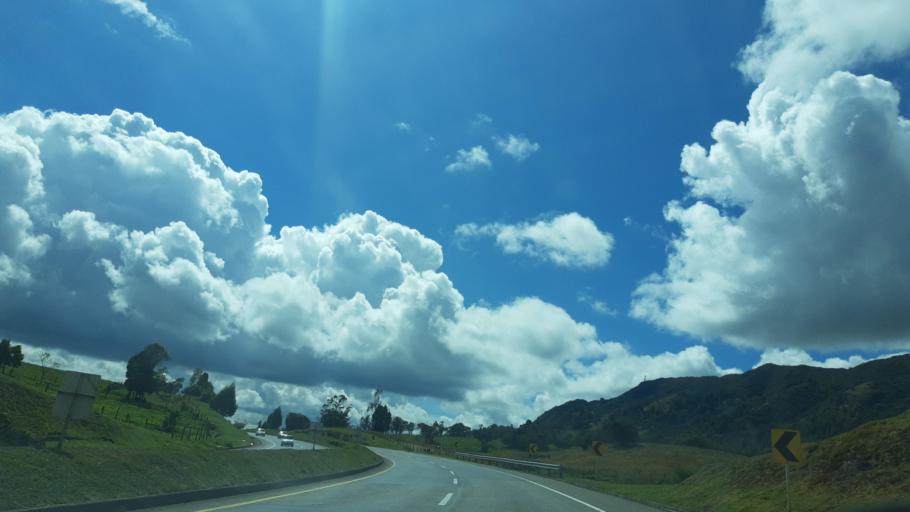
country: CO
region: Boyaca
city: Ventaquemada
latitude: 5.3973
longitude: -73.4935
